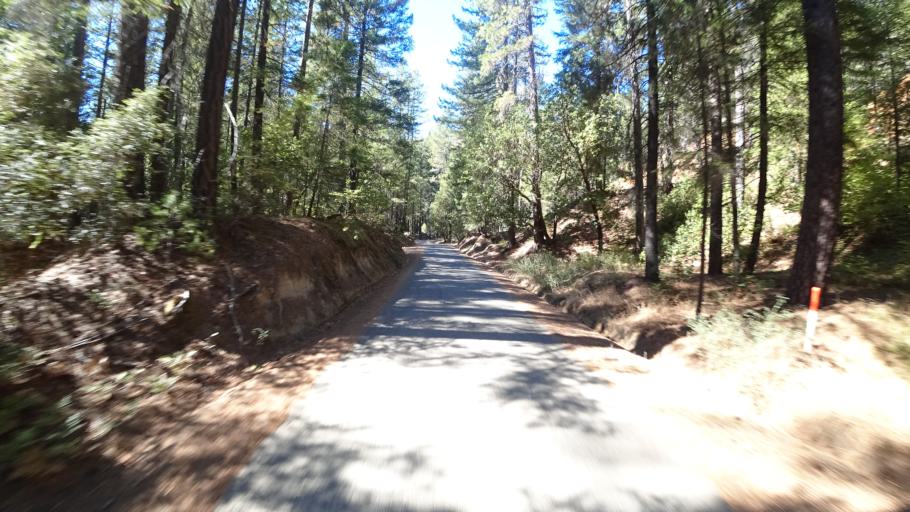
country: US
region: California
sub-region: Siskiyou County
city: Happy Camp
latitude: 41.3155
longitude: -123.1818
